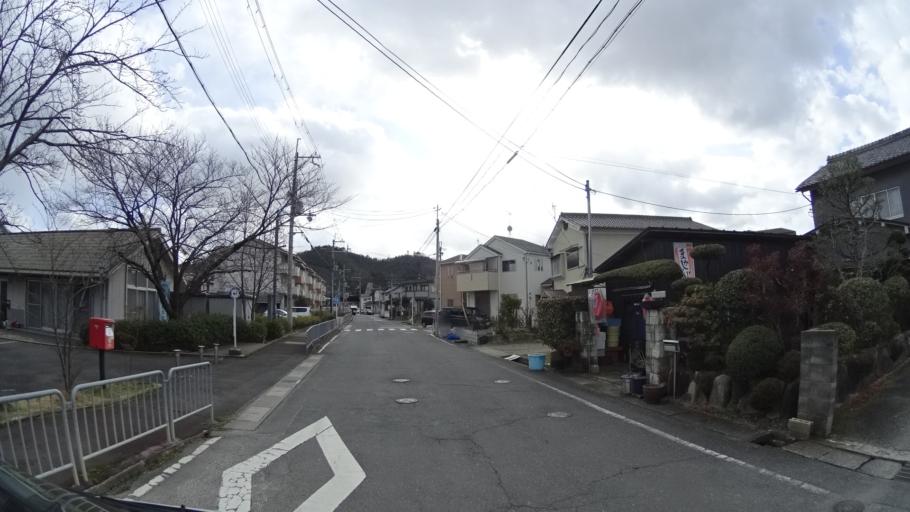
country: JP
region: Kyoto
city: Kameoka
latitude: 35.0171
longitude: 135.5704
